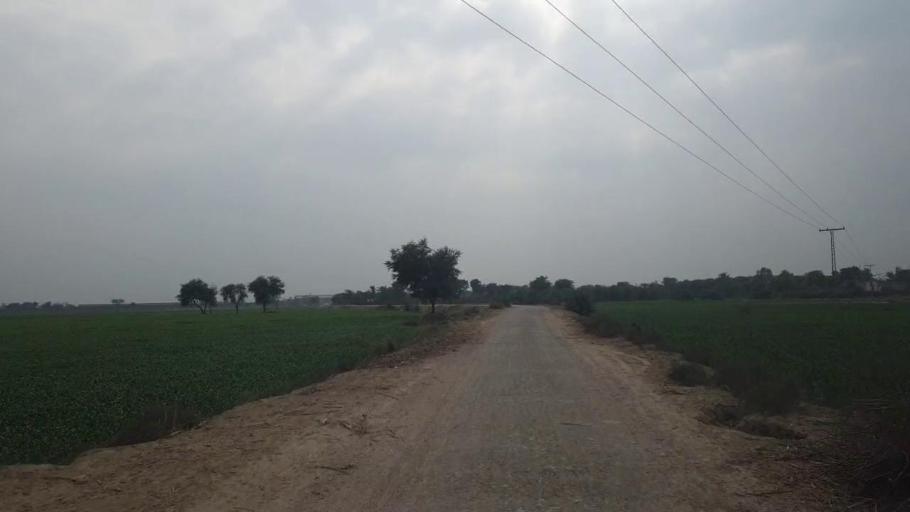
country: PK
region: Sindh
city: Shahdadpur
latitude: 25.9423
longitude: 68.7021
